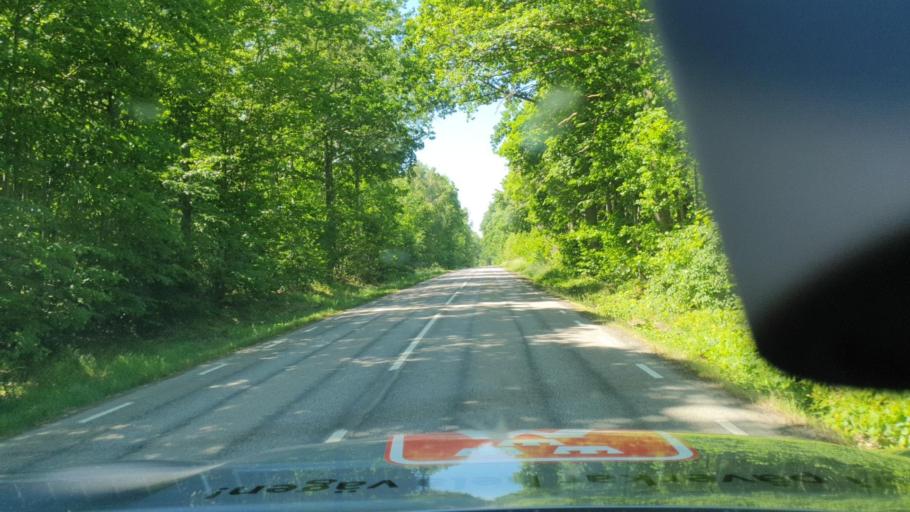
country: SE
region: Kalmar
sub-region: Torsas Kommun
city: Torsas
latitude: 56.4344
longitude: 15.8574
